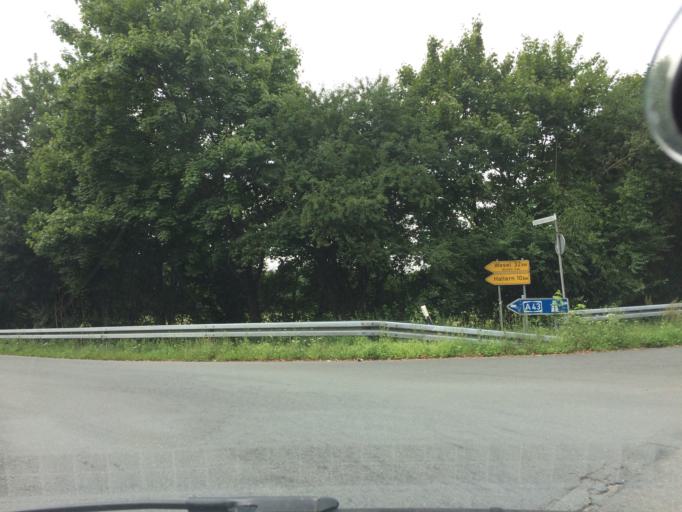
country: DE
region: North Rhine-Westphalia
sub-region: Regierungsbezirk Munster
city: Klein Reken
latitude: 51.7207
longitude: 7.0430
